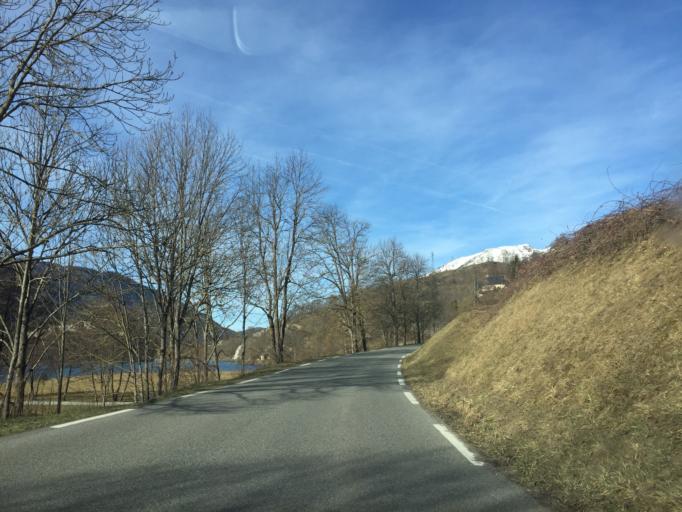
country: FR
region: Midi-Pyrenees
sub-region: Departement des Hautes-Pyrenees
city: Saint-Lary-Soulan
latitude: 42.8022
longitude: 0.4110
